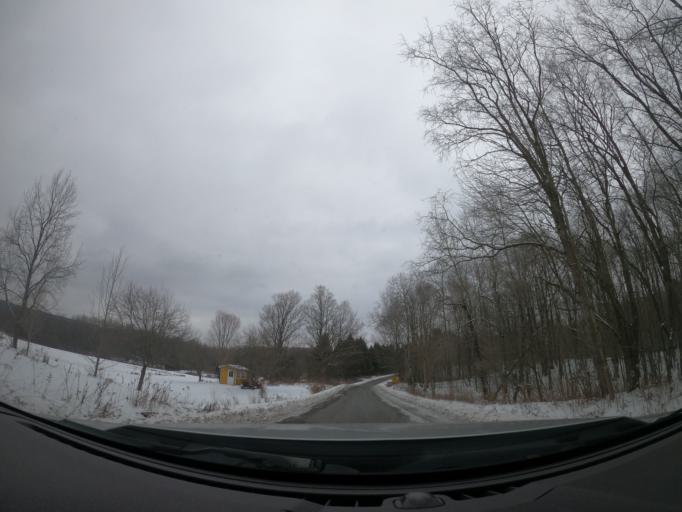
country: US
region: New York
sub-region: Cayuga County
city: Moravia
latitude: 42.7341
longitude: -76.2951
